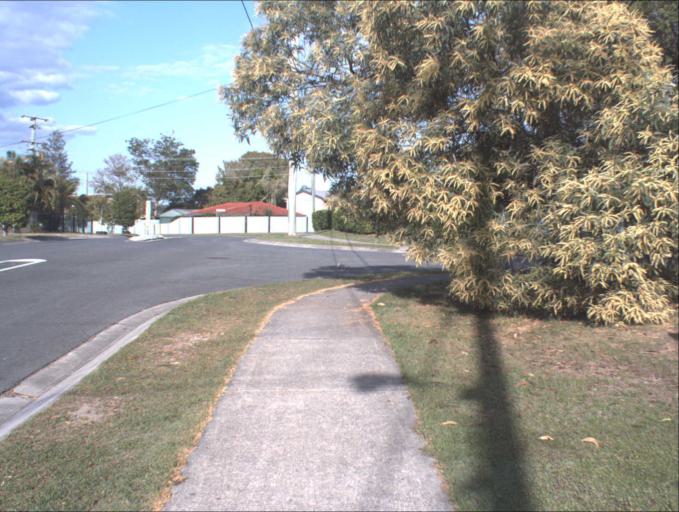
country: AU
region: Queensland
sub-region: Logan
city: Waterford West
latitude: -27.6864
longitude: 153.0988
